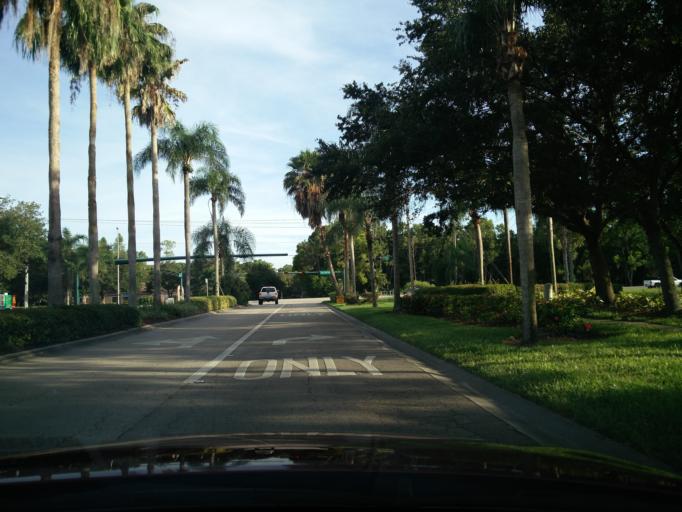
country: US
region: Florida
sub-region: Collier County
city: Vineyards
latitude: 26.2126
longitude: -81.7308
